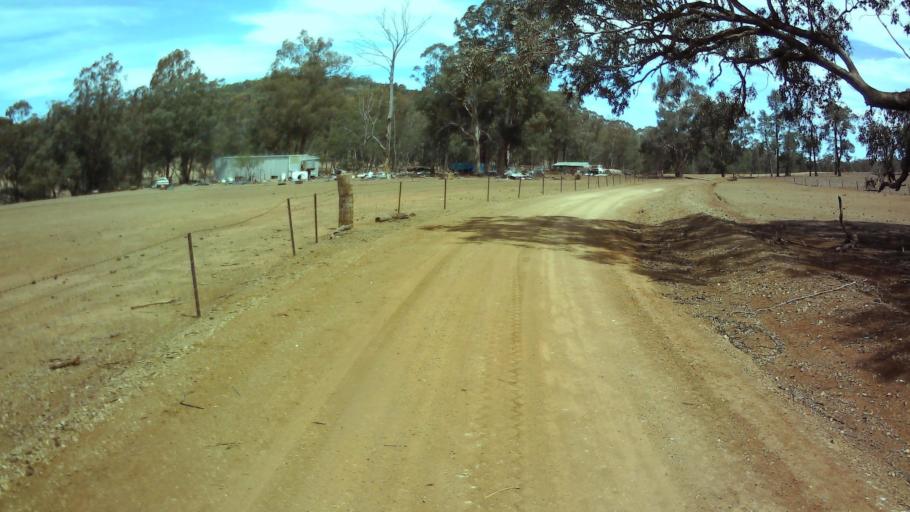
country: AU
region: New South Wales
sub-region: Weddin
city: Grenfell
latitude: -33.7925
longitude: 148.1602
